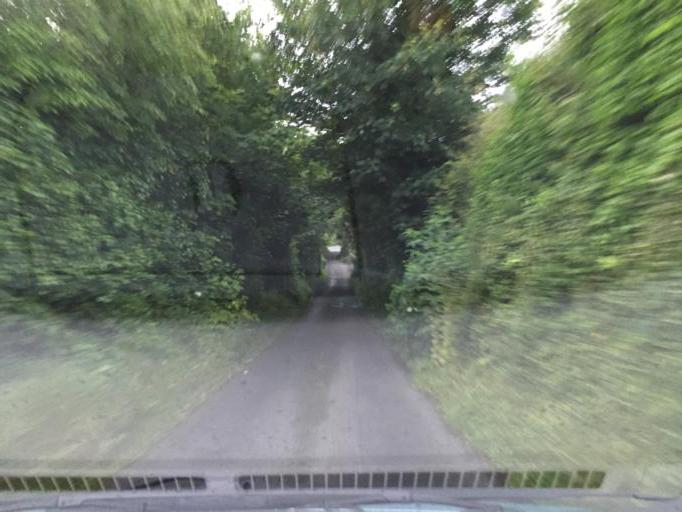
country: IE
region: Connaught
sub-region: Sligo
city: Strandhill
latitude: 54.2488
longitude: -8.5805
